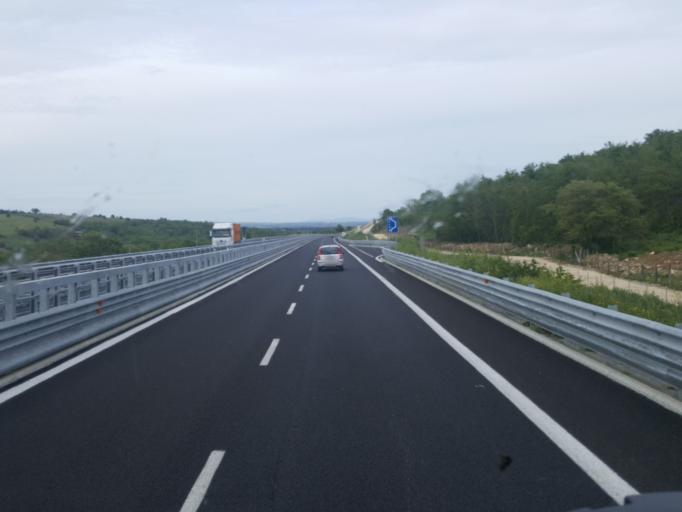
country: IT
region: Latium
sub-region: Provincia di Viterbo
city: Monte Romano
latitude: 42.2888
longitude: 11.9382
